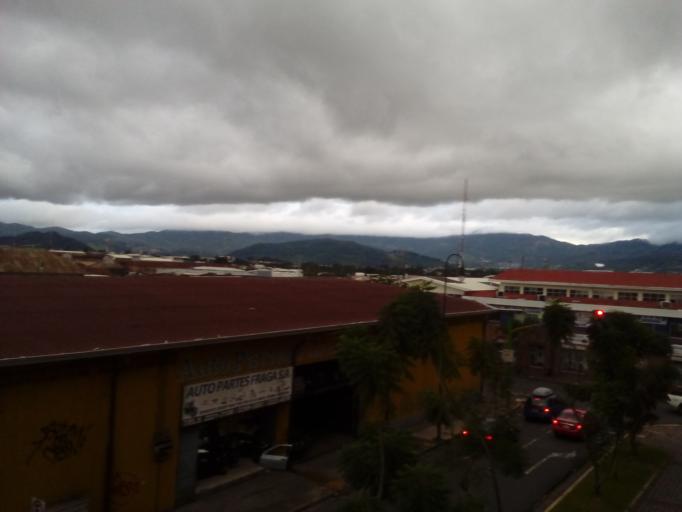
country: CR
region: San Jose
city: San Jose
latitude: 9.9267
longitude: -84.0789
